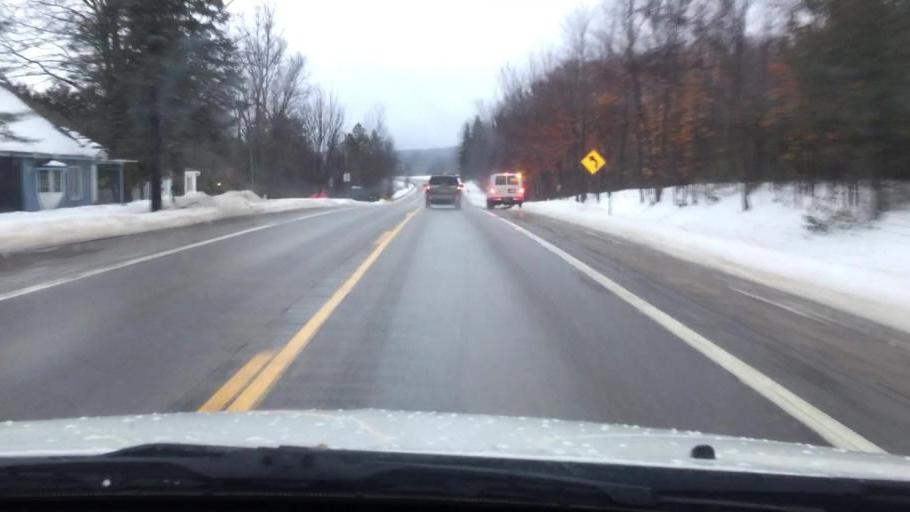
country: US
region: Michigan
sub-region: Charlevoix County
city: East Jordan
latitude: 45.1888
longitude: -85.1649
